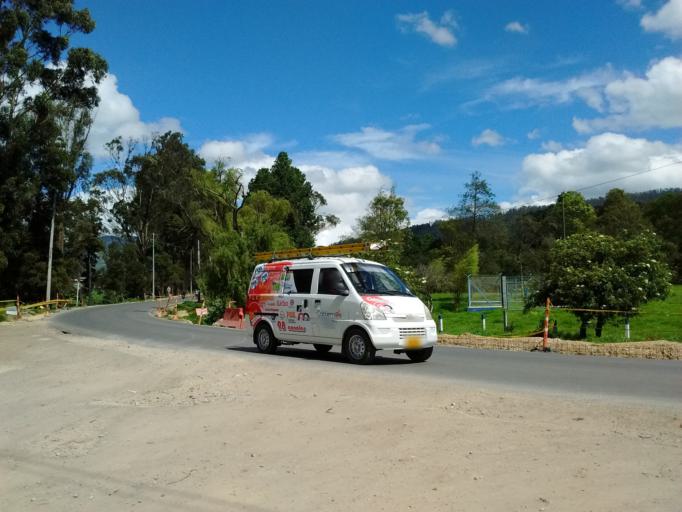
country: CO
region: Cundinamarca
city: Facatativa
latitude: 4.8091
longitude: -74.3161
